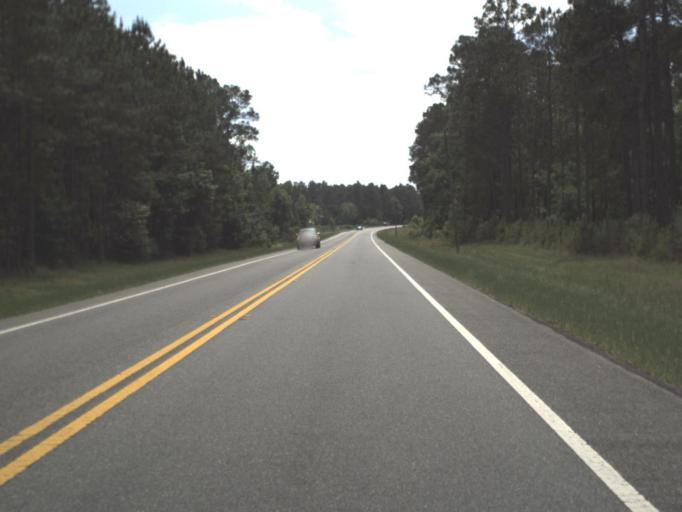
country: US
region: Florida
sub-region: Calhoun County
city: Blountstown
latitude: 30.3934
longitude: -85.0857
